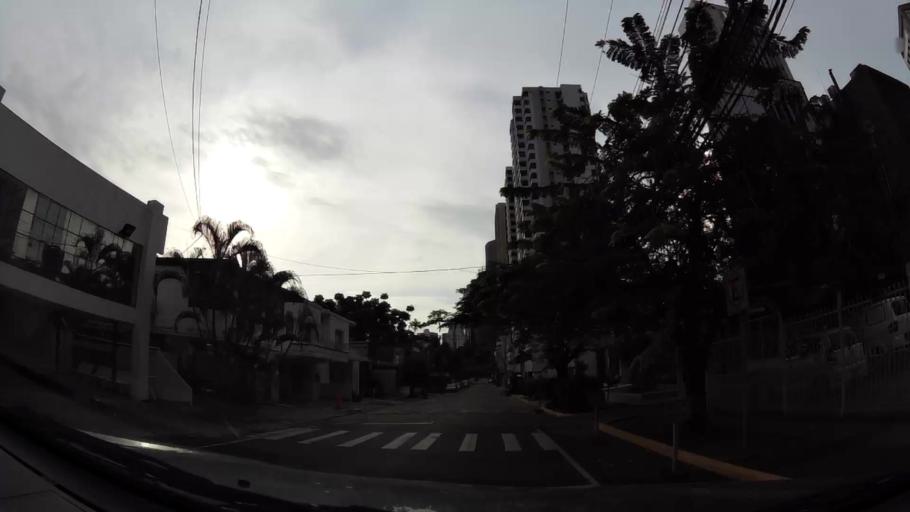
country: PA
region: Panama
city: Panama
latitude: 8.9815
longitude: -79.5192
